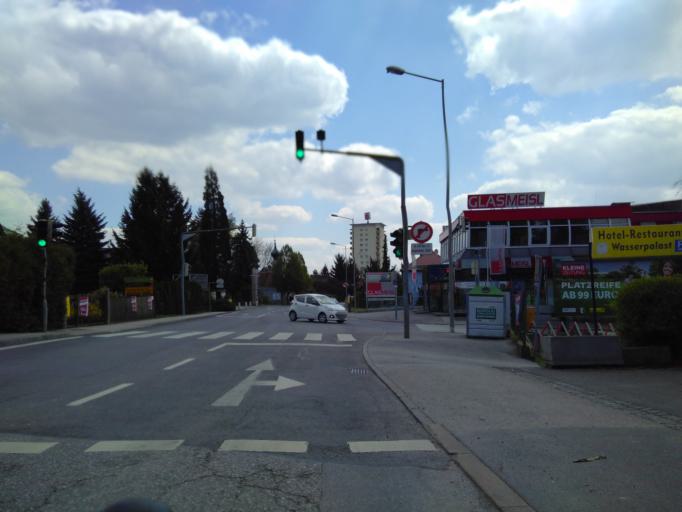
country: AT
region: Styria
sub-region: Politischer Bezirk Graz-Umgebung
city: Feldkirchen bei Graz
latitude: 47.0226
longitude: 15.4696
